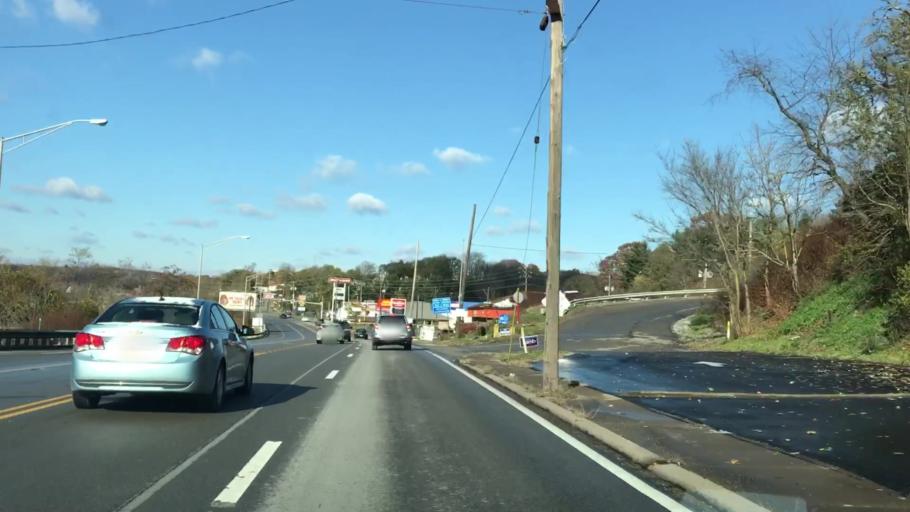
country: US
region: Pennsylvania
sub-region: Beaver County
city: Monaca
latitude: 40.6976
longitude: -80.2696
